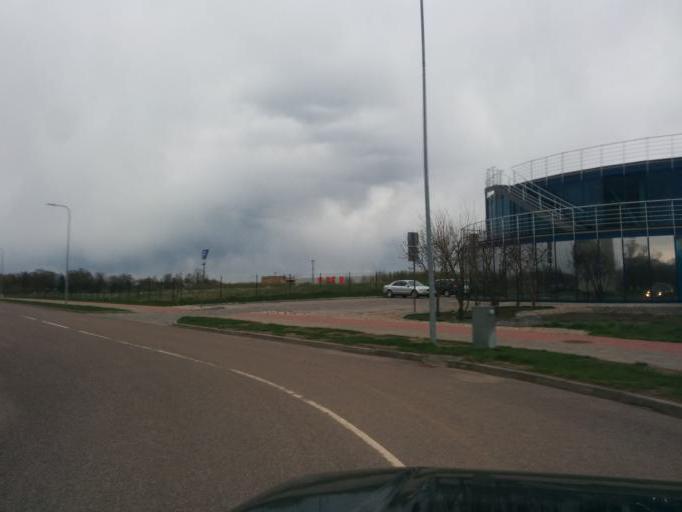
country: LV
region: Jelgava
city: Jelgava
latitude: 56.6512
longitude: 23.7395
